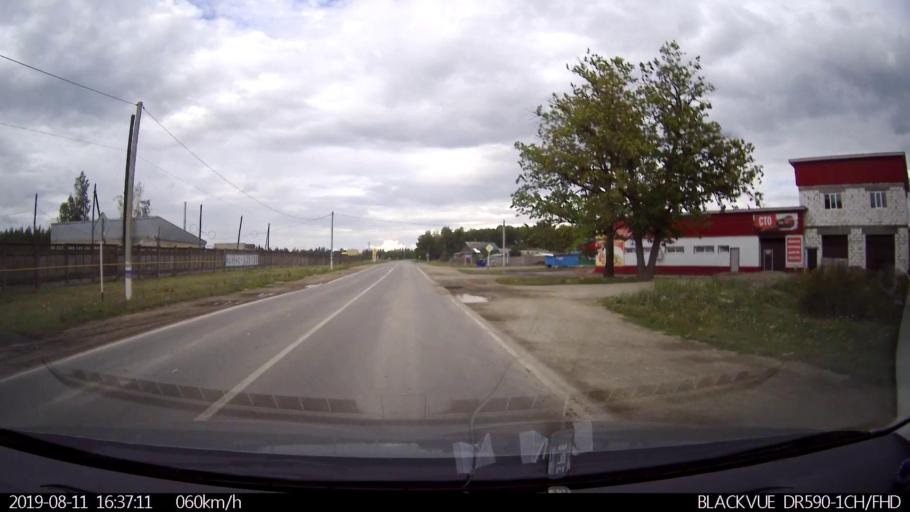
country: RU
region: Ulyanovsk
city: Mayna
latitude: 54.1253
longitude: 47.6128
